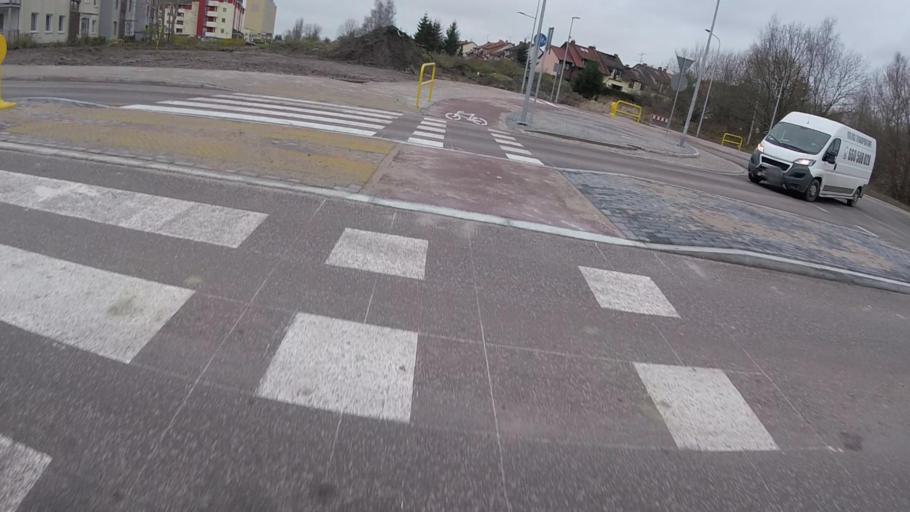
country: PL
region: West Pomeranian Voivodeship
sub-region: Koszalin
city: Koszalin
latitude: 54.1924
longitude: 16.2227
